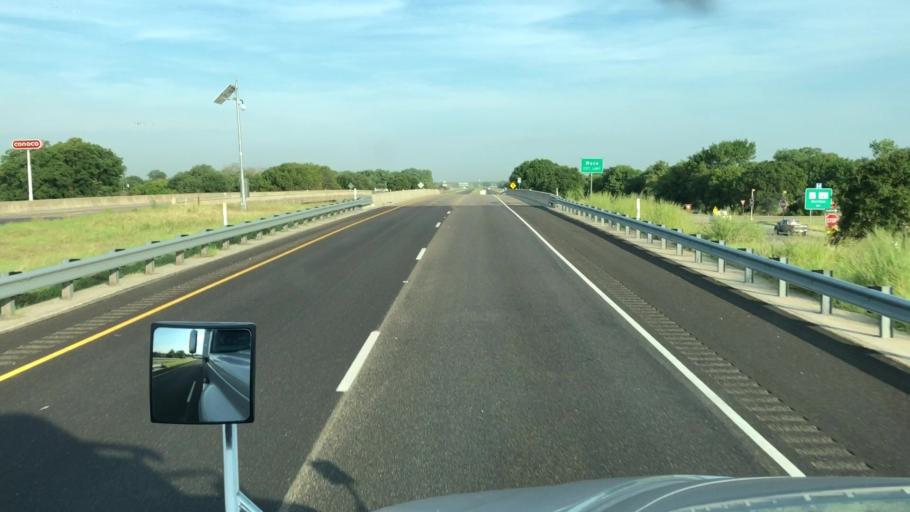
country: US
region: Texas
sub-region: McLennan County
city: Bellmead
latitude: 31.5469
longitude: -97.0686
